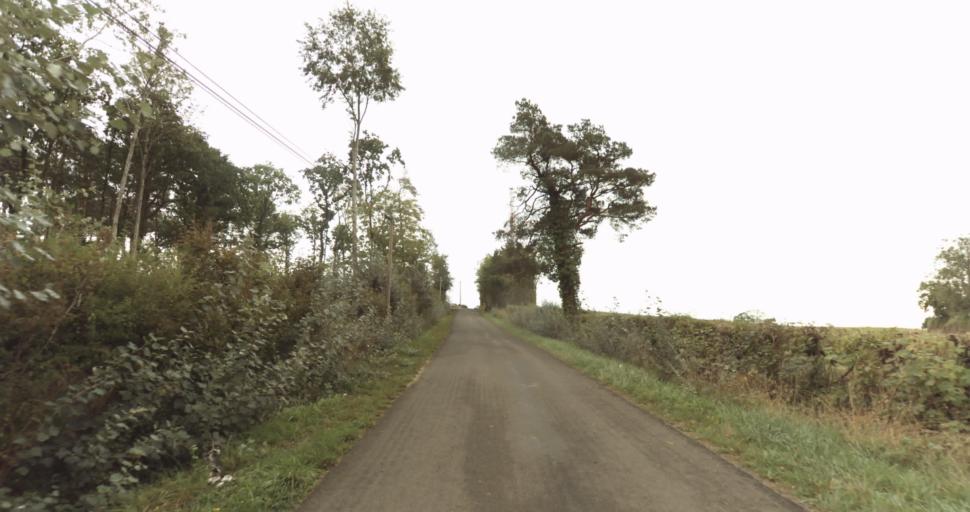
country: FR
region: Lower Normandy
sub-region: Departement de l'Orne
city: Gace
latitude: 48.7175
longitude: 0.3184
